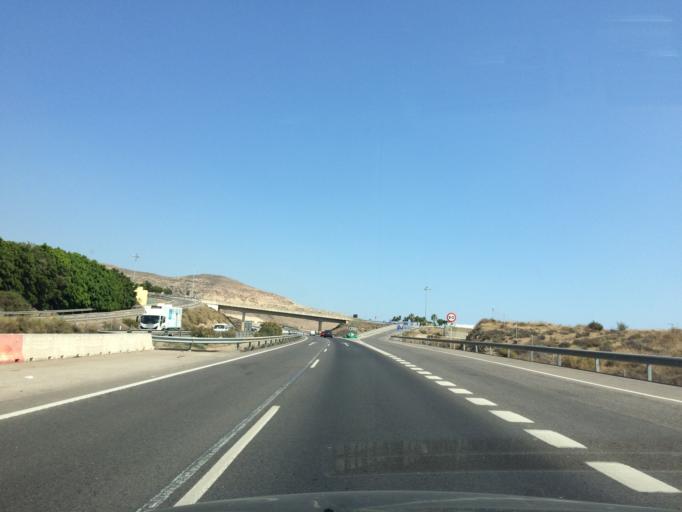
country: ES
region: Andalusia
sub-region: Provincia de Almeria
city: Vicar
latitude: 36.8129
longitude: -2.6561
